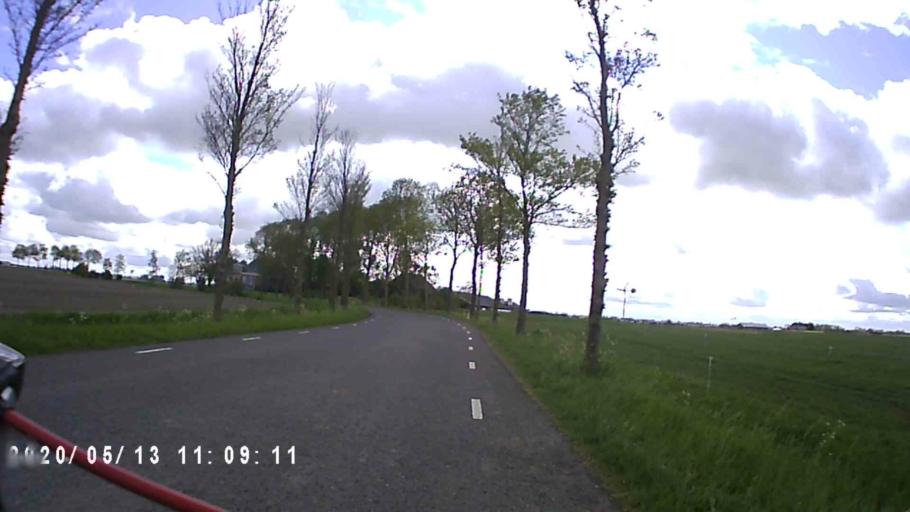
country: NL
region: Groningen
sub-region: Gemeente Zuidhorn
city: Grijpskerk
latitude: 53.2947
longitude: 6.3407
